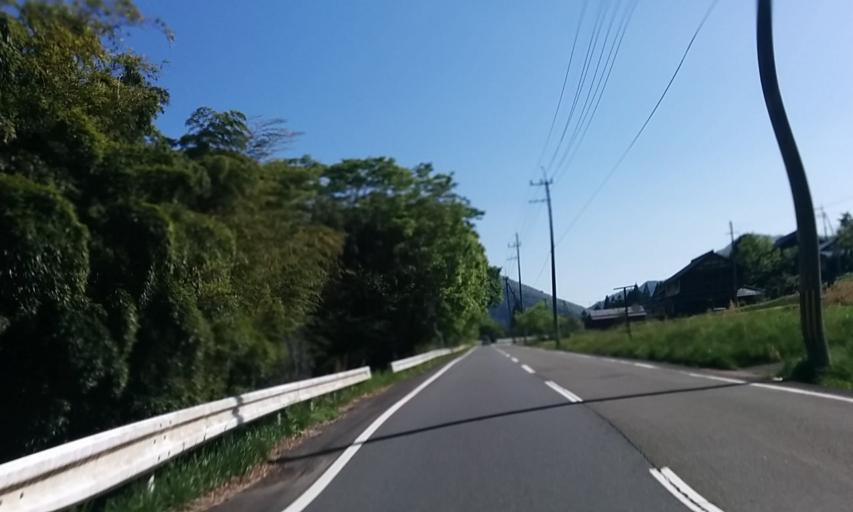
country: JP
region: Kyoto
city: Ayabe
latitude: 35.2605
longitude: 135.4289
